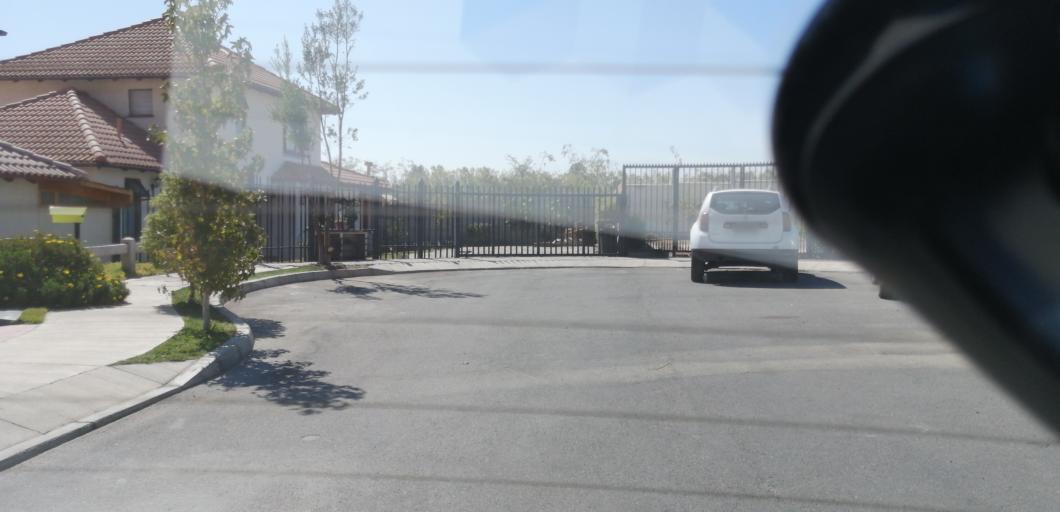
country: CL
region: Santiago Metropolitan
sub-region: Provincia de Santiago
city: Lo Prado
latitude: -33.4513
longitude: -70.8234
